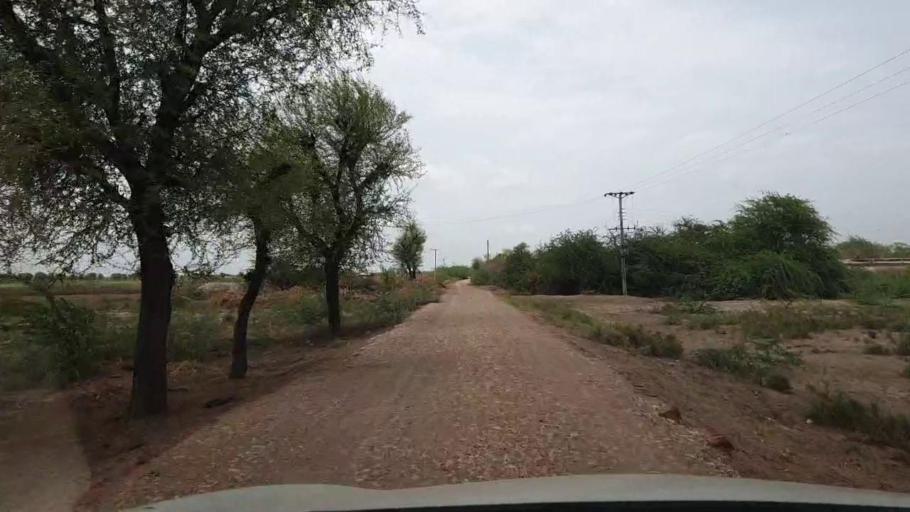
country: PK
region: Sindh
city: Chambar
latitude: 25.2123
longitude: 68.7616
